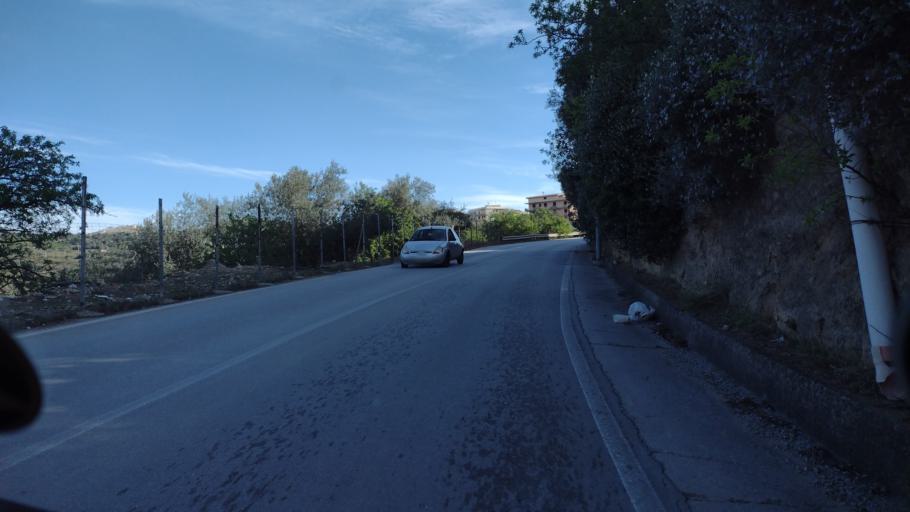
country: IT
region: Sicily
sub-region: Provincia di Siracusa
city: Noto
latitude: 36.8979
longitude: 15.0638
